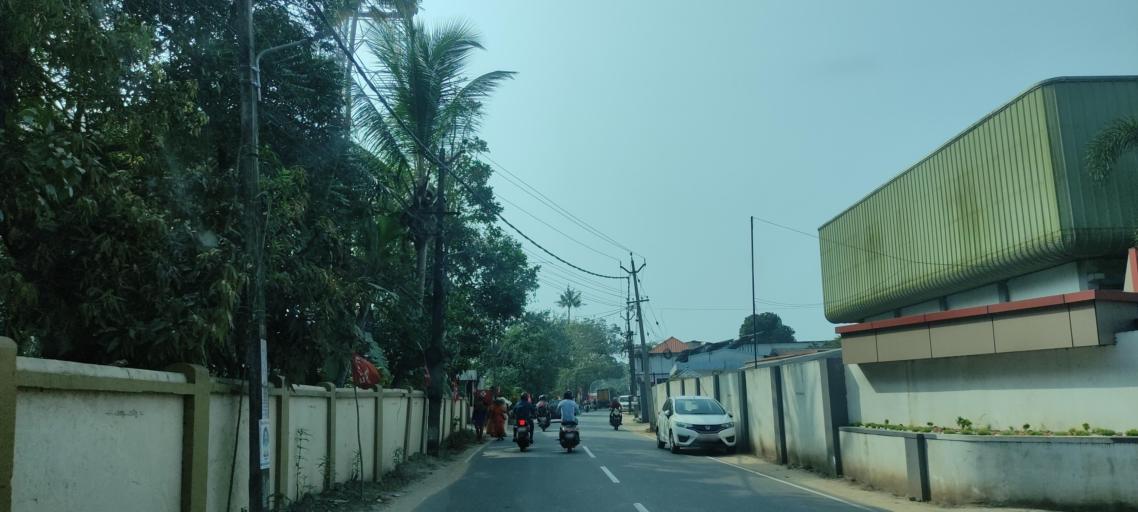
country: IN
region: Kerala
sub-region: Alappuzha
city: Vayalar
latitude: 9.6954
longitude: 76.3265
